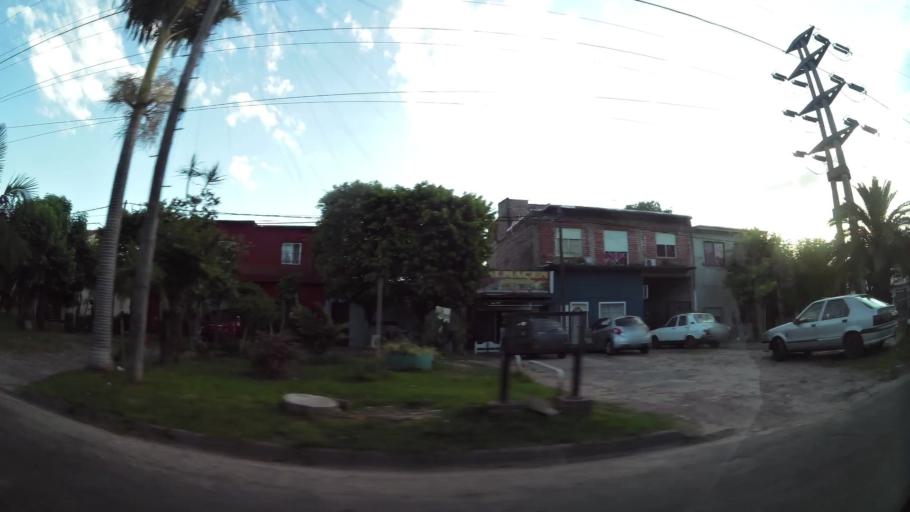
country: AR
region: Buenos Aires
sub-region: Partido de Tigre
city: Tigre
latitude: -34.4548
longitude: -58.5661
